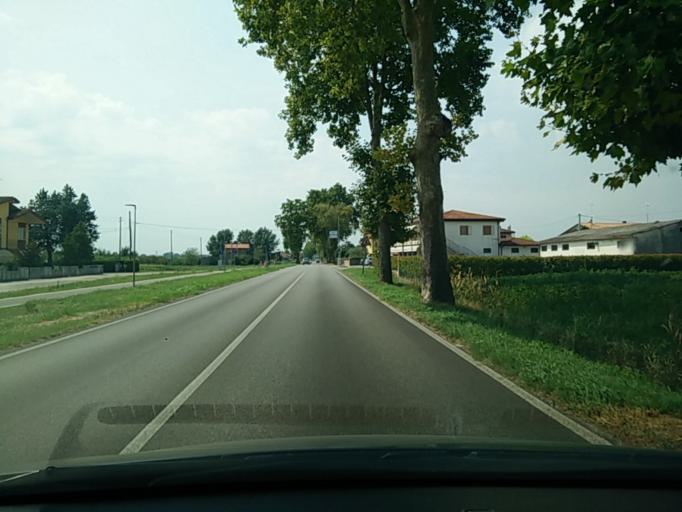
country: IT
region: Veneto
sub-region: Provincia di Venezia
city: Crepaldo
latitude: 45.5898
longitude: 12.6883
